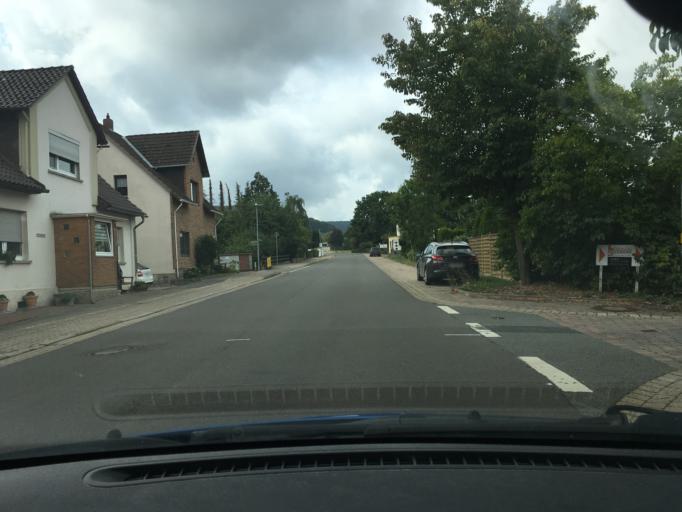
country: DE
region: Lower Saxony
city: Bad Munder am Deister
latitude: 52.1965
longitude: 9.4135
